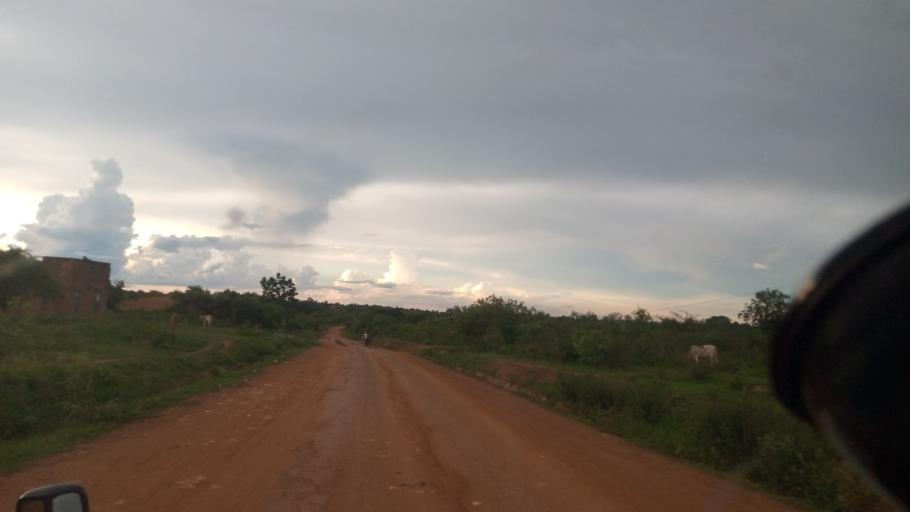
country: UG
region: Northern Region
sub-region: Kole District
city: Kole
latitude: 2.4917
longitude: 32.9347
